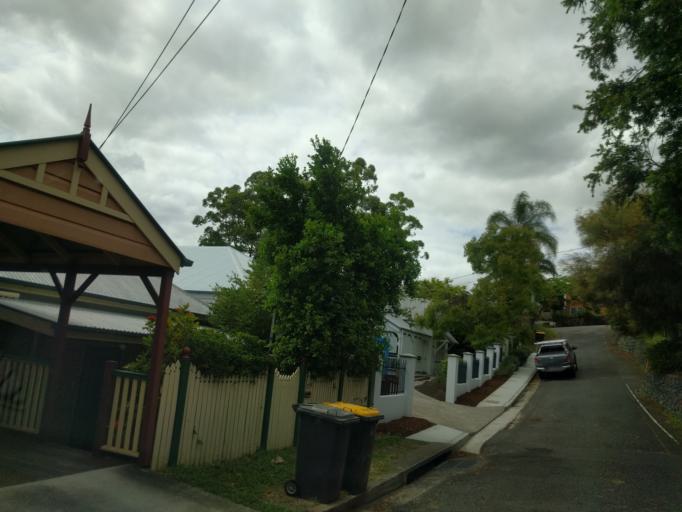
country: AU
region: Queensland
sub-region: Brisbane
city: Milton
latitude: -27.4668
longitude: 152.9937
